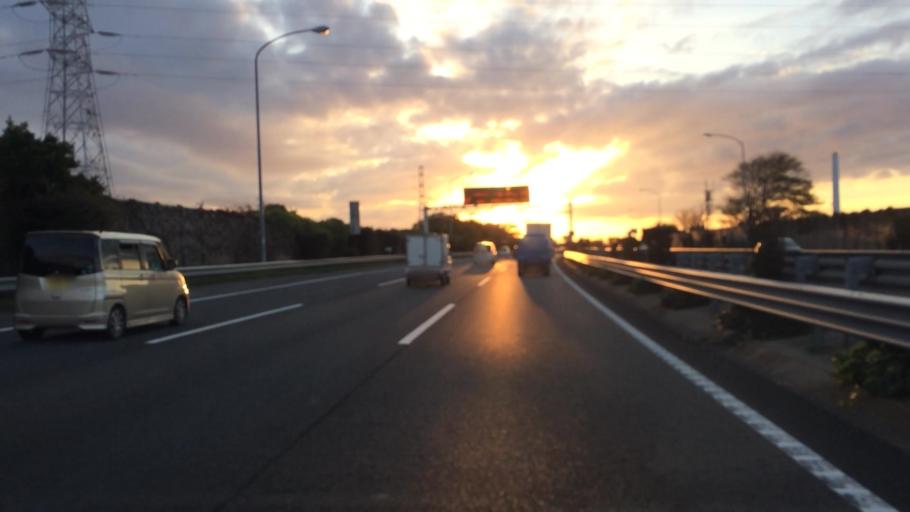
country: JP
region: Chiba
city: Yotsukaido
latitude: 35.6733
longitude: 140.1288
